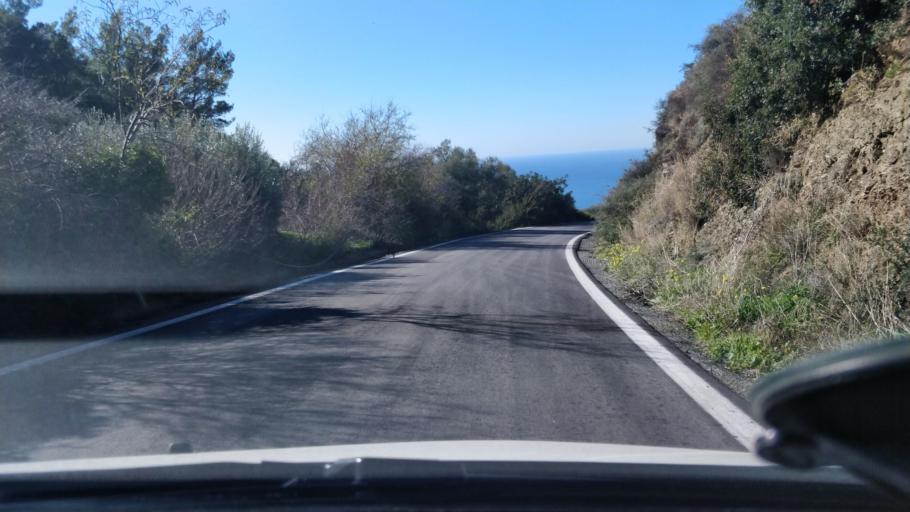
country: GR
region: Crete
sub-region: Nomos Irakleiou
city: Arkalochori
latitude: 35.0056
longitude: 25.4411
